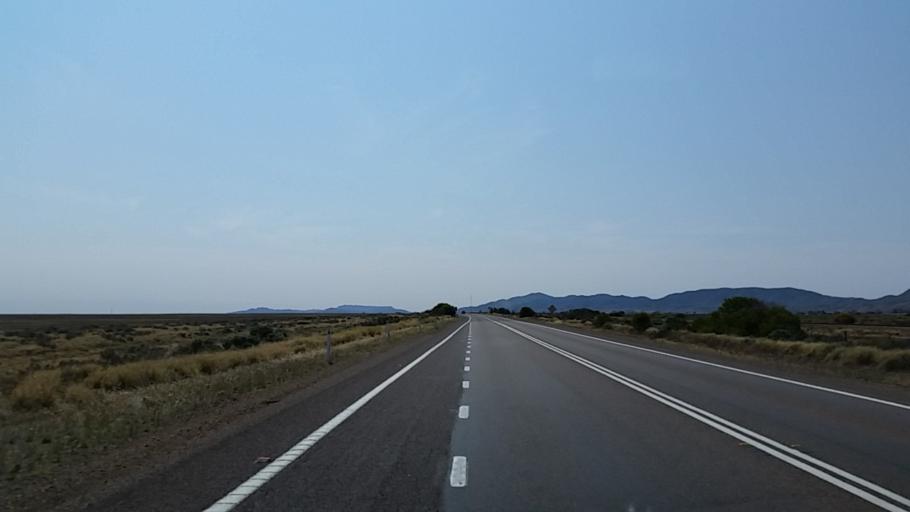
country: AU
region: South Australia
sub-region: Port Augusta
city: Port Augusta
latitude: -32.7098
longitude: 137.9412
